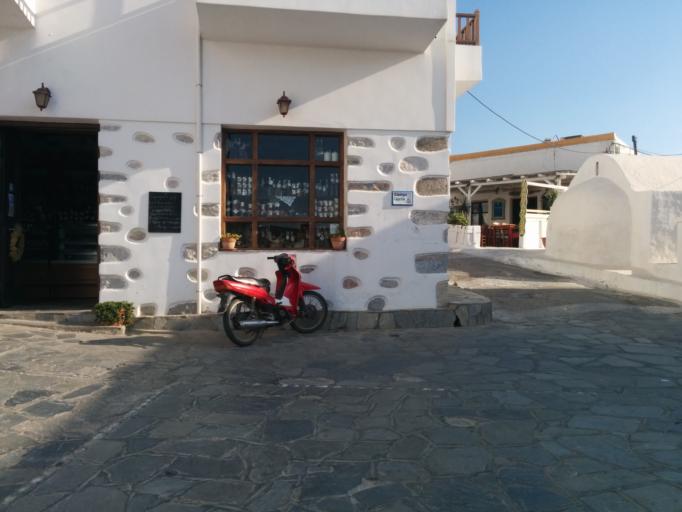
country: GR
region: South Aegean
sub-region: Nomos Dodekanisou
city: Astypalaia
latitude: 36.5453
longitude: 26.3532
